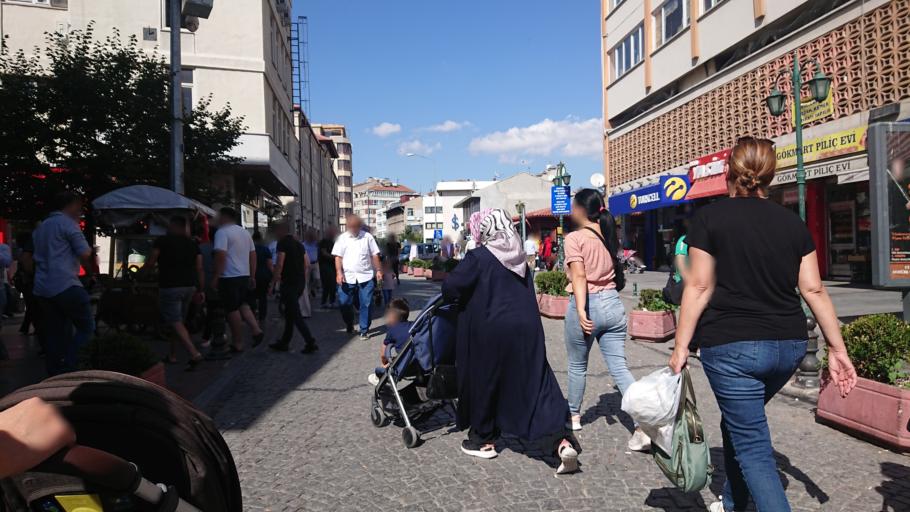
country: TR
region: Eskisehir
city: Eskisehir
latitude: 39.7749
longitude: 30.5193
